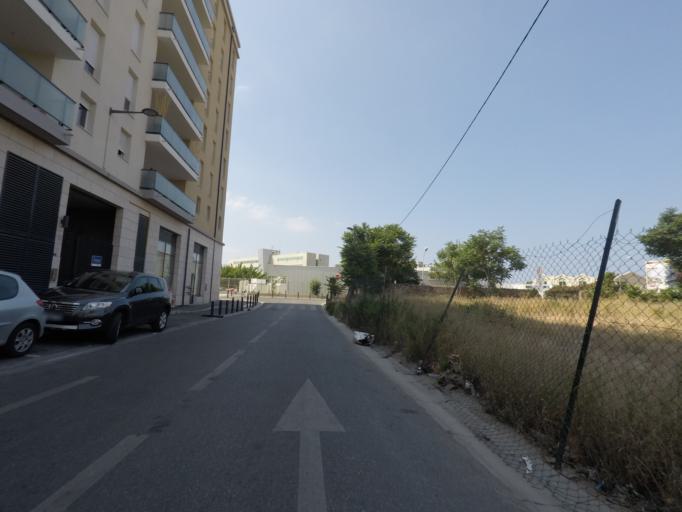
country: FR
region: Provence-Alpes-Cote d'Azur
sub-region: Departement des Bouches-du-Rhone
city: Marseille 10
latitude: 43.2782
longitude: 5.4059
